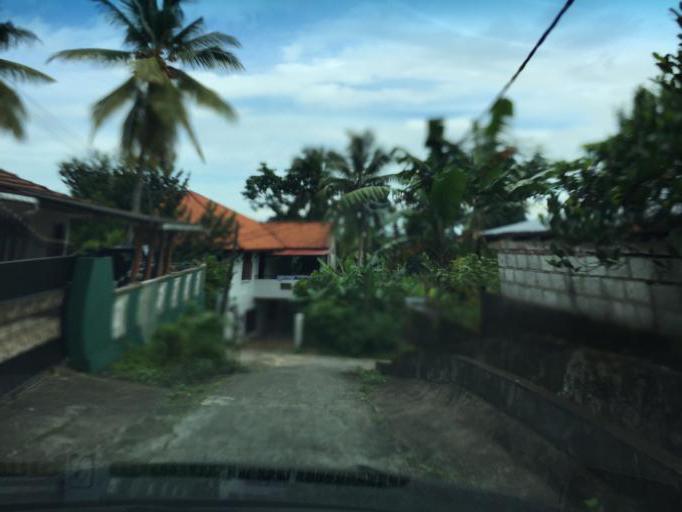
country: LK
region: Western
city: Horana South
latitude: 6.7150
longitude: 80.0592
